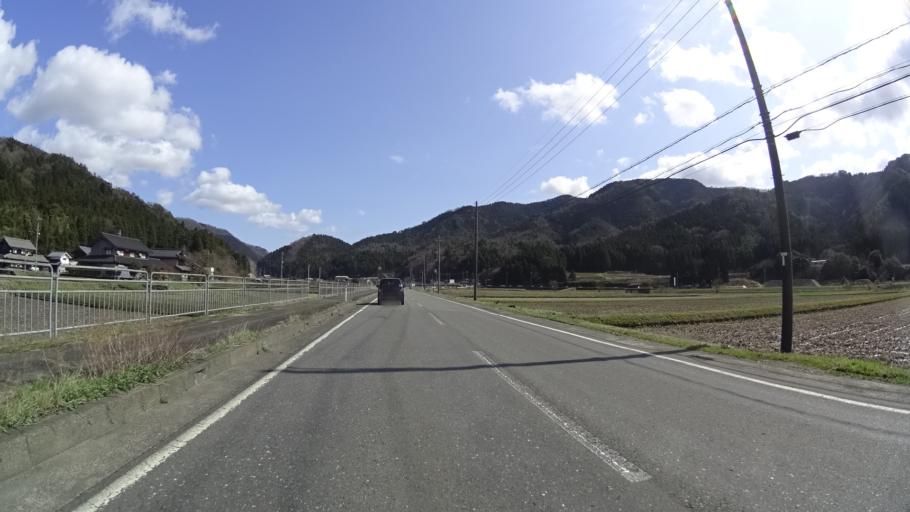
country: JP
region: Fukui
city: Obama
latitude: 35.4530
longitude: 135.8824
